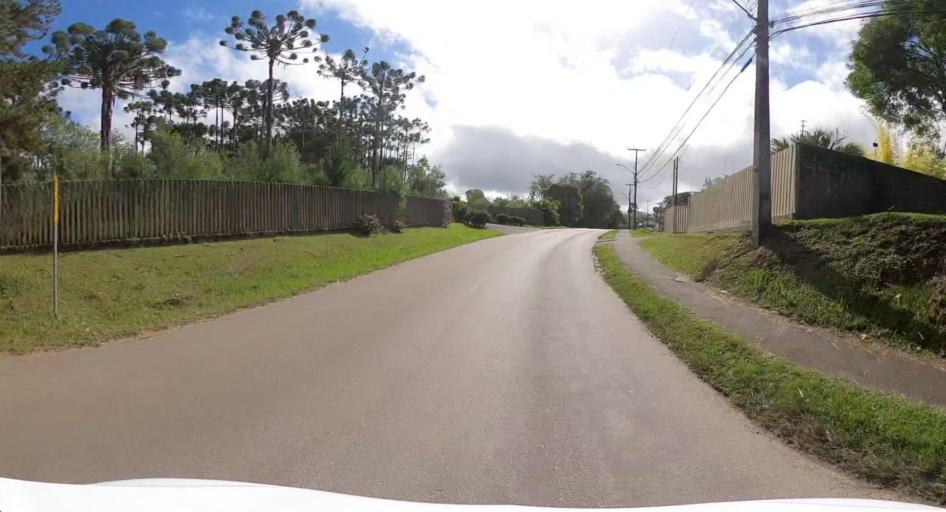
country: BR
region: Parana
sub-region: Campina Grande Do Sul
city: Campina Grande do Sul
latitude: -25.3033
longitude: -49.0518
